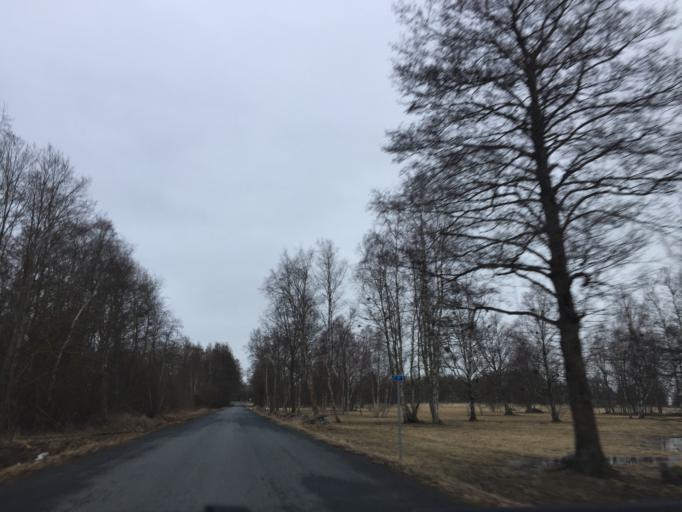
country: EE
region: Laeaene
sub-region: Haapsalu linn
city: Haapsalu
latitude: 58.7872
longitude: 23.4784
